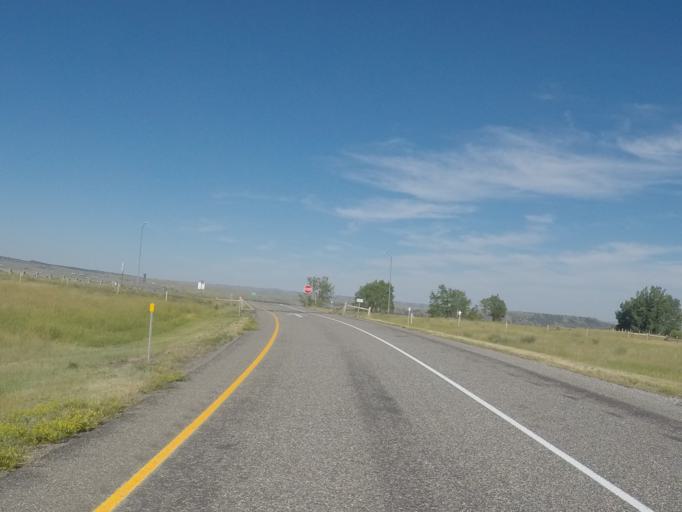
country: US
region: Montana
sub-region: Sweet Grass County
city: Big Timber
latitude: 45.8311
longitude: -109.9094
